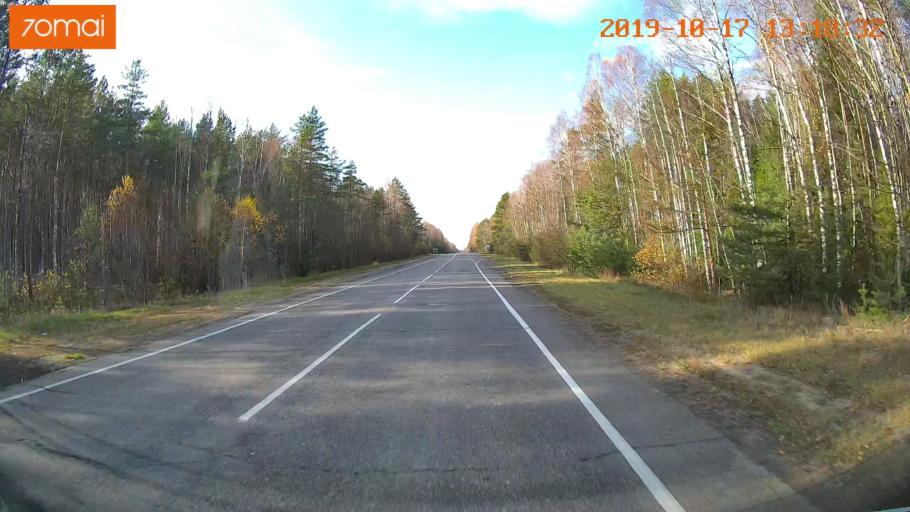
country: RU
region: Rjazan
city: Gus'-Zheleznyy
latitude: 55.0636
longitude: 41.0957
